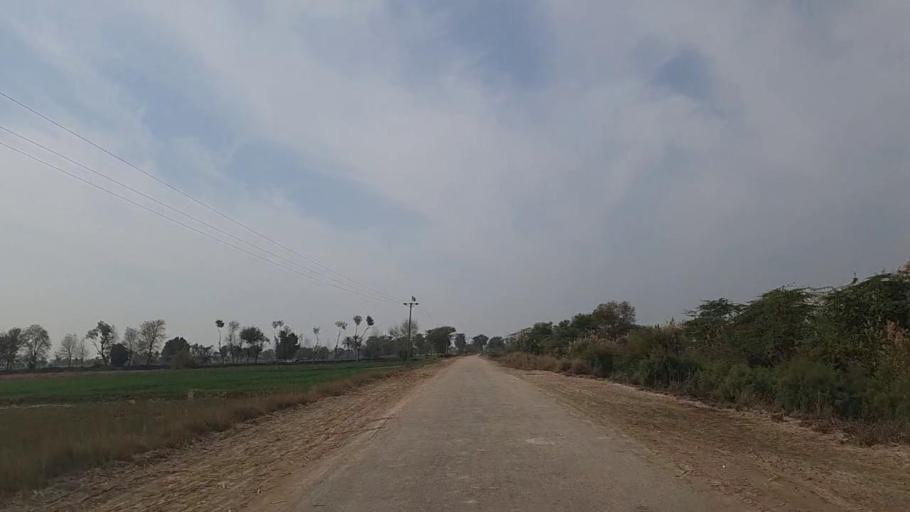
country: PK
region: Sindh
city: Daur
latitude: 26.4514
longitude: 68.4293
